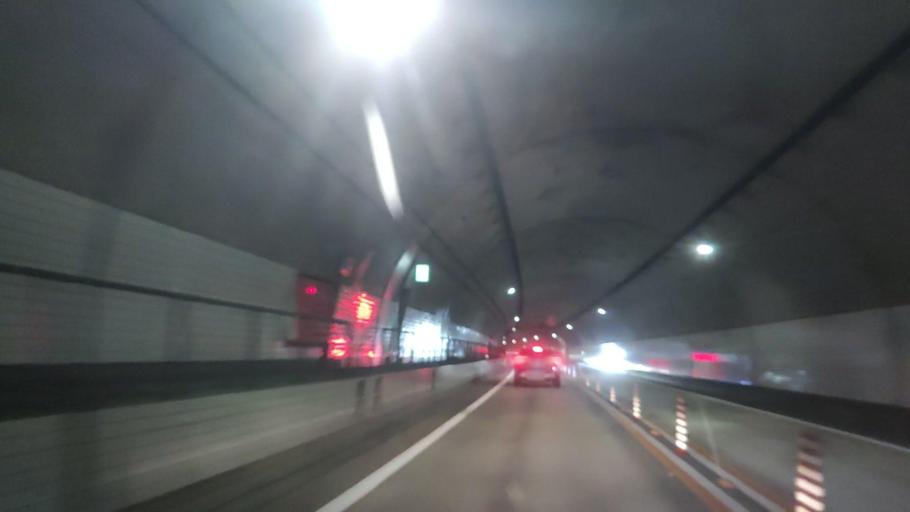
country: JP
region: Kyoto
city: Miyazu
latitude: 35.5571
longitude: 135.1255
